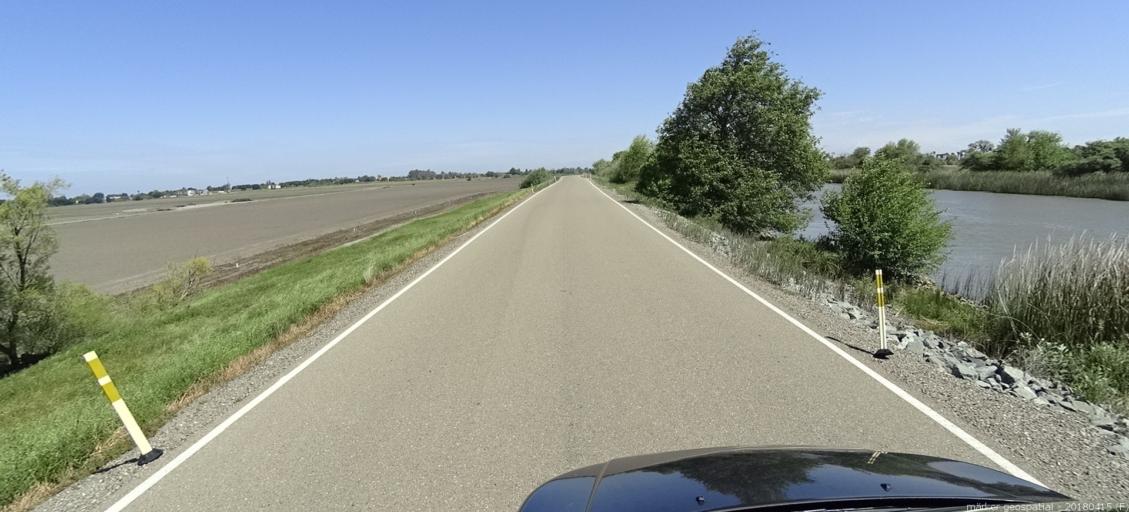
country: US
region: California
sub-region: Solano County
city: Rio Vista
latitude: 38.1489
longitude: -121.5996
